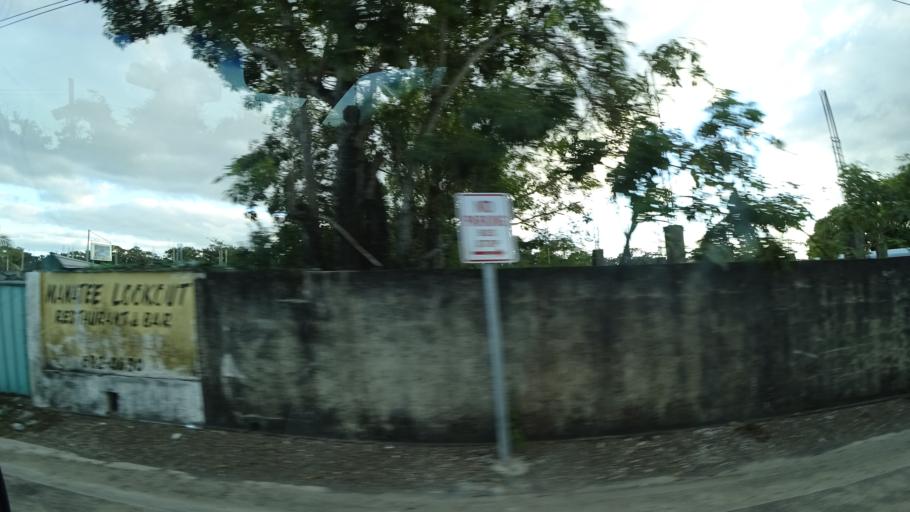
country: BZ
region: Belize
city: Belize City
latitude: 17.5450
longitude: -88.2832
